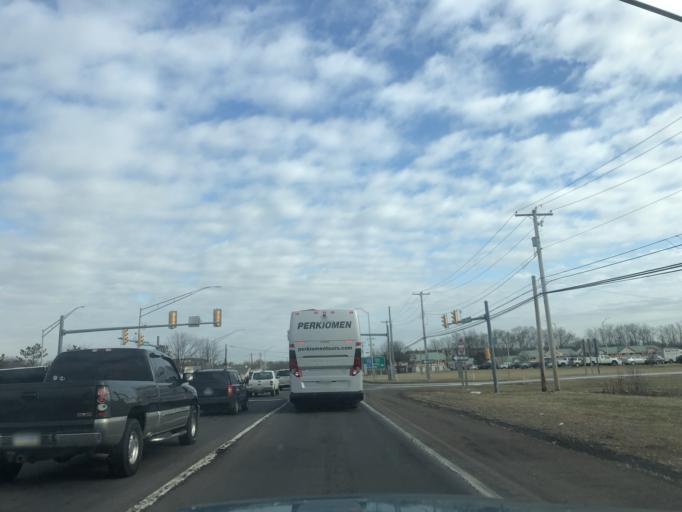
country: US
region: Pennsylvania
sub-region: Bucks County
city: Spinnerstown
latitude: 40.4347
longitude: -75.4214
